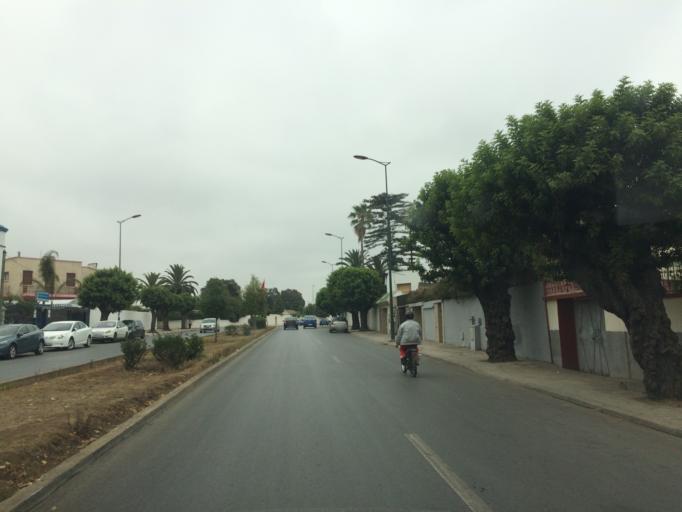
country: MA
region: Rabat-Sale-Zemmour-Zaer
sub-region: Rabat
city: Rabat
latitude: 33.9905
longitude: -6.8180
